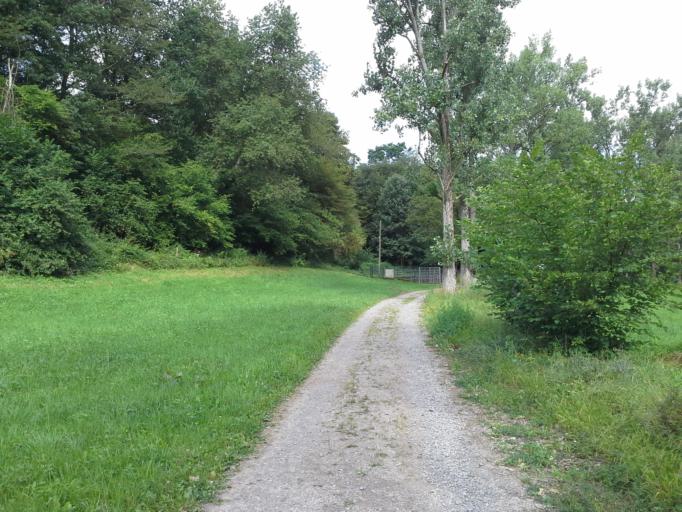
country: DE
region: Baden-Wuerttemberg
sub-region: Karlsruhe Region
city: Dobel
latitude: 48.8607
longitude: 8.5286
